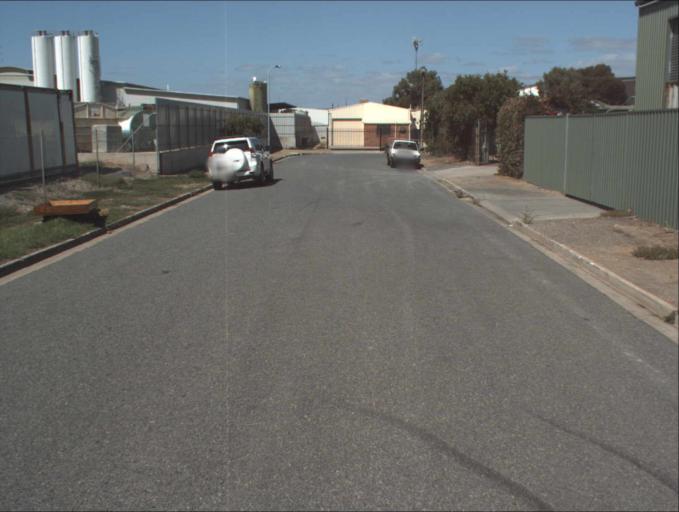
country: AU
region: South Australia
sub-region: Charles Sturt
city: Woodville North
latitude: -34.8433
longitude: 138.5562
